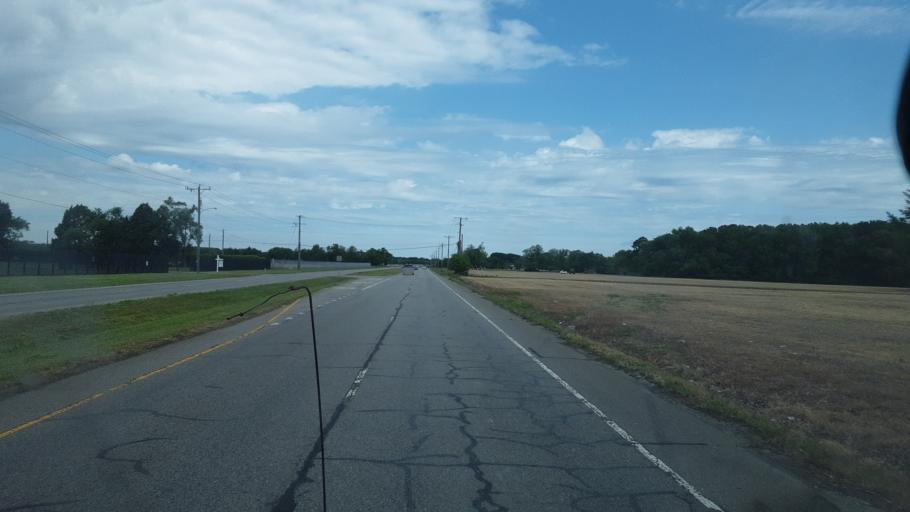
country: US
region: Virginia
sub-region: City of Virginia Beach
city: Virginia Beach
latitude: 36.8124
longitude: -76.0052
